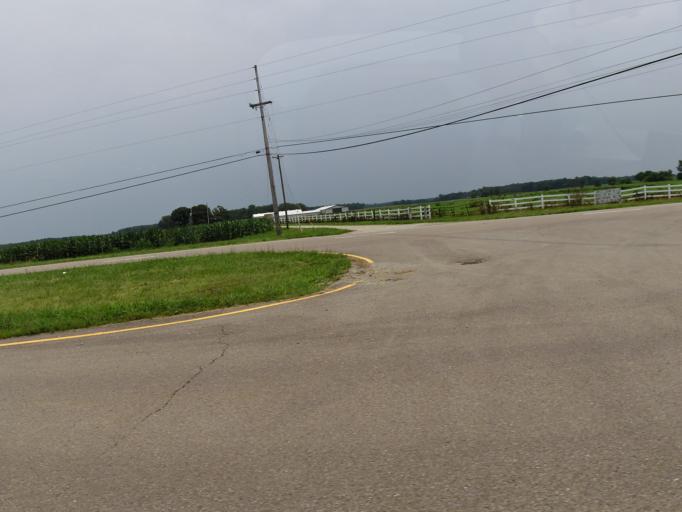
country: US
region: Ohio
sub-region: Greene County
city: Bellbrook
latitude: 39.6177
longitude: -83.9941
